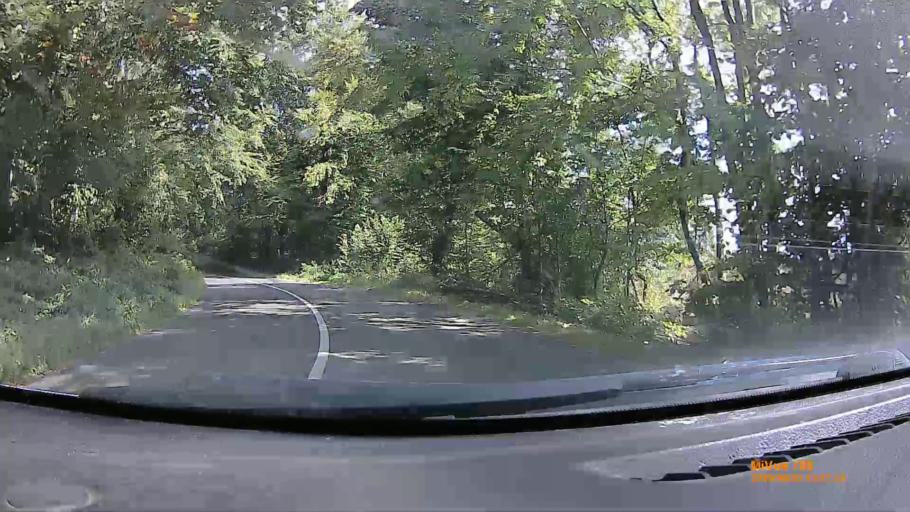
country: HU
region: Borsod-Abauj-Zemplen
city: Saly
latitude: 48.0638
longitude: 20.5764
